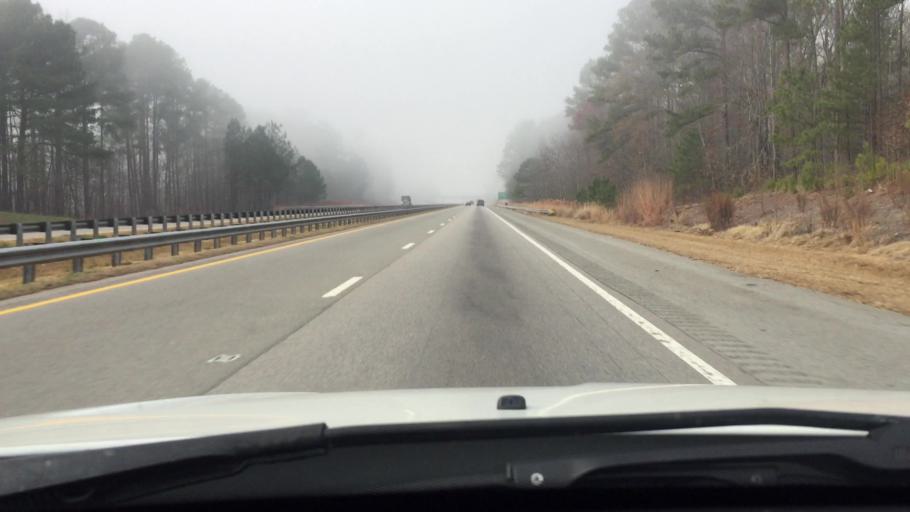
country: US
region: North Carolina
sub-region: Wake County
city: Holly Springs
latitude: 35.6719
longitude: -78.9235
